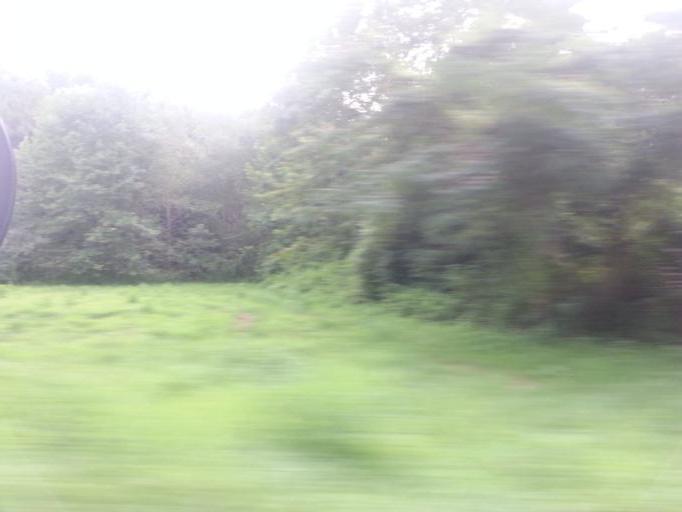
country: US
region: Tennessee
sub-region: Campbell County
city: Caryville
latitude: 36.2048
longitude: -84.3068
